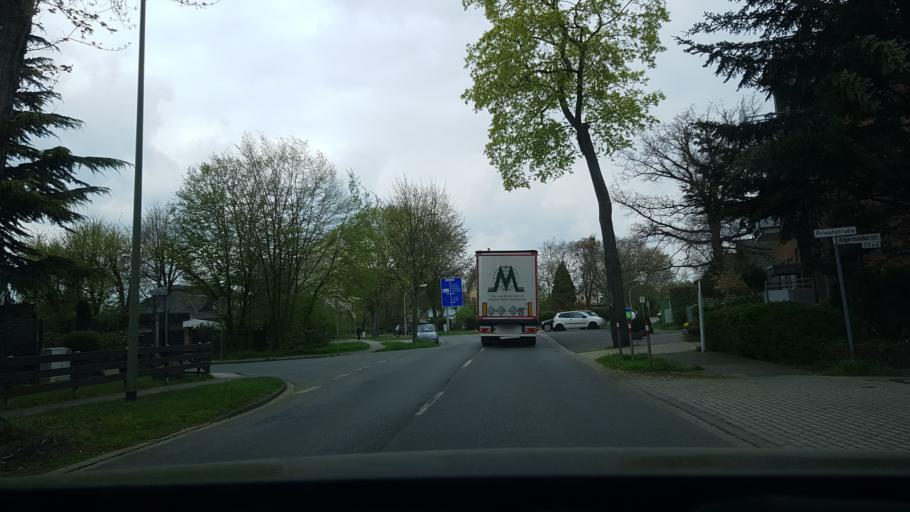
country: DE
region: North Rhine-Westphalia
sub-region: Regierungsbezirk Dusseldorf
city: Hochfeld
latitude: 51.3496
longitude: 6.7877
